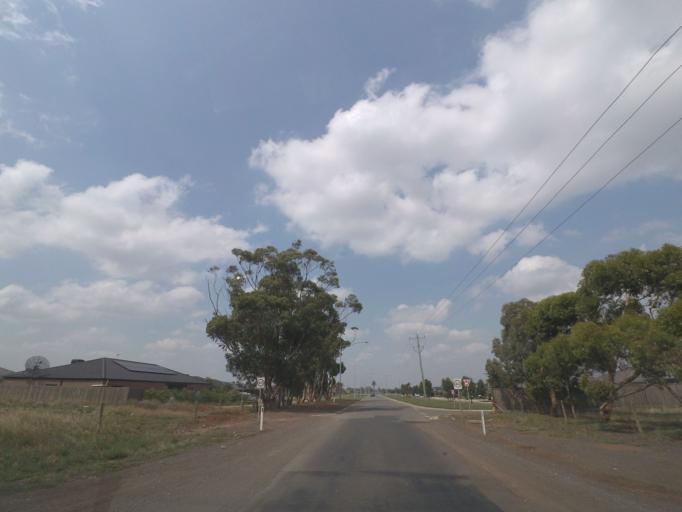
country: AU
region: Victoria
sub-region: Melton
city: Melton West
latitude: -37.6634
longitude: 144.5538
